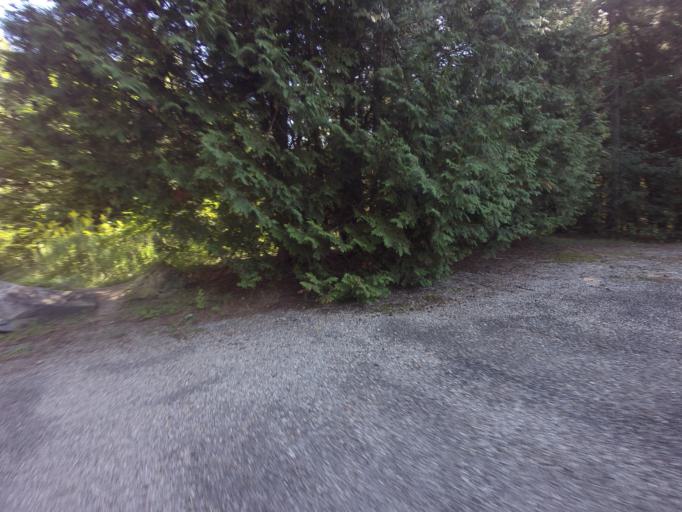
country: CA
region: Ontario
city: Waterloo
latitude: 43.6796
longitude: -80.4413
